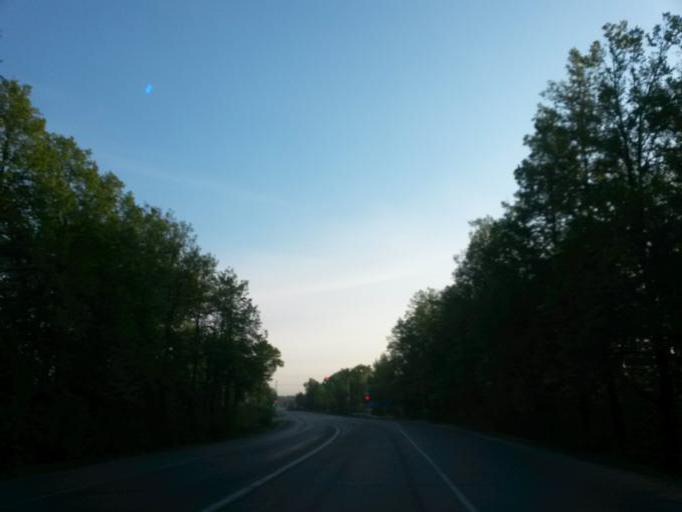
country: RU
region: Moskovskaya
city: Stolbovaya
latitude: 55.2562
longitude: 37.5082
